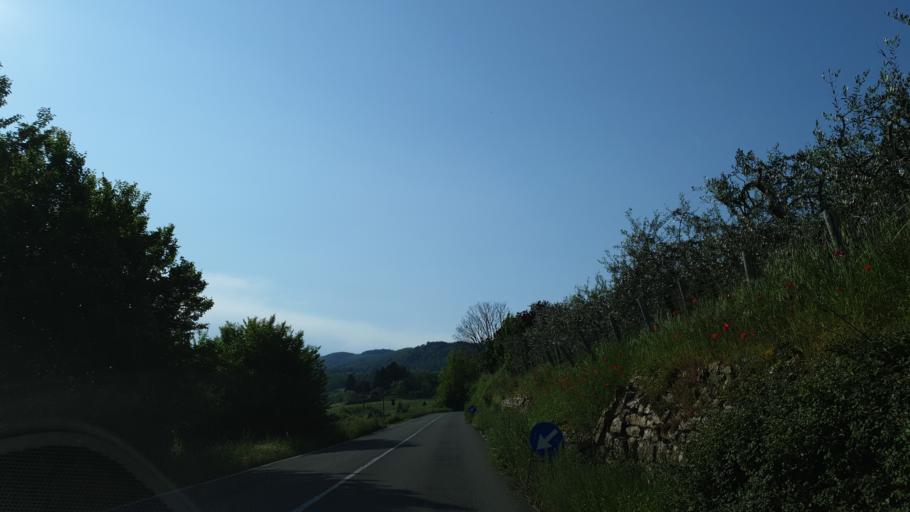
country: IT
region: Tuscany
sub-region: Province of Arezzo
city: Castel San Niccolo
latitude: 43.7627
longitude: 11.7077
